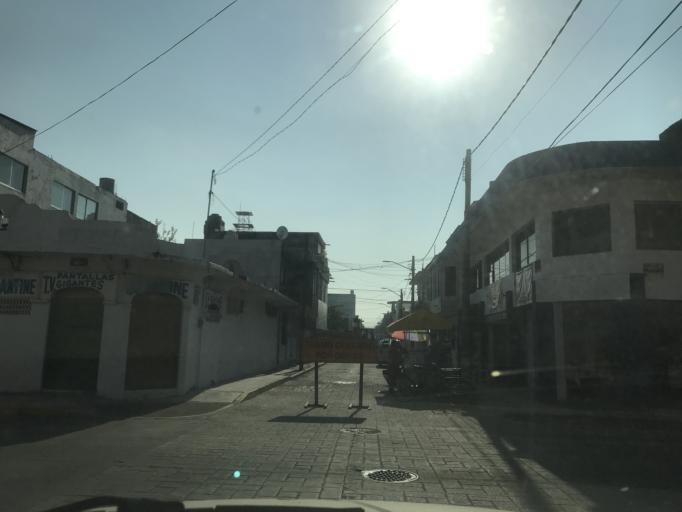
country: MX
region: Colima
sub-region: Manzanillo
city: Manzanillo
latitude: 19.0498
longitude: -104.3186
